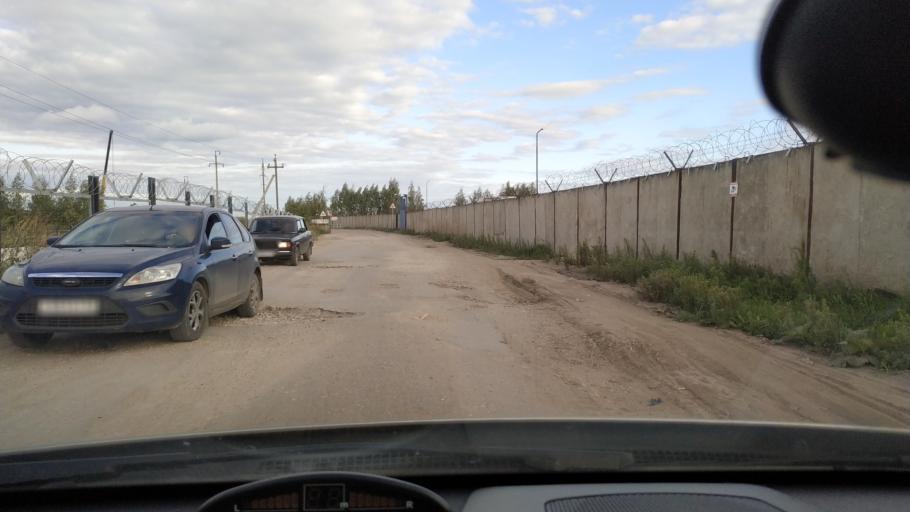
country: RU
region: Rjazan
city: Polyany
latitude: 54.5774
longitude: 39.8424
